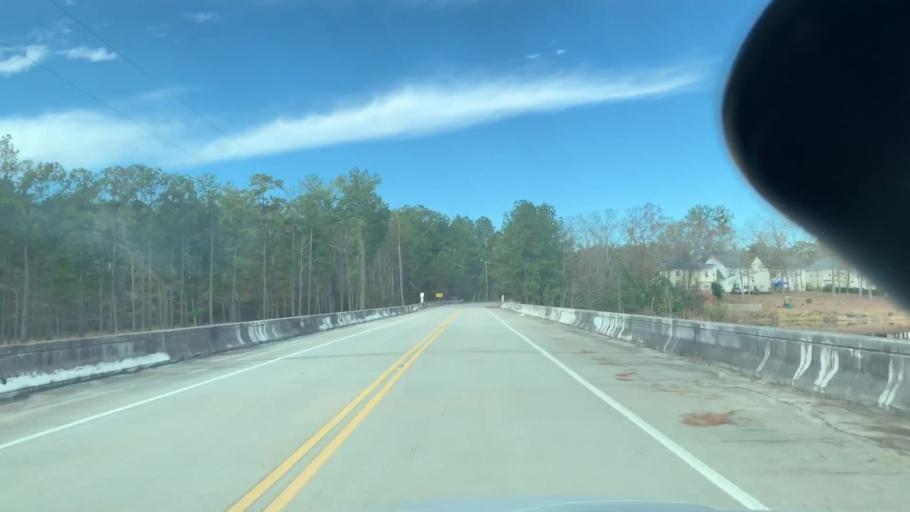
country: US
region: South Carolina
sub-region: Richland County
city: Woodfield
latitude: 34.0742
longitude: -80.9284
